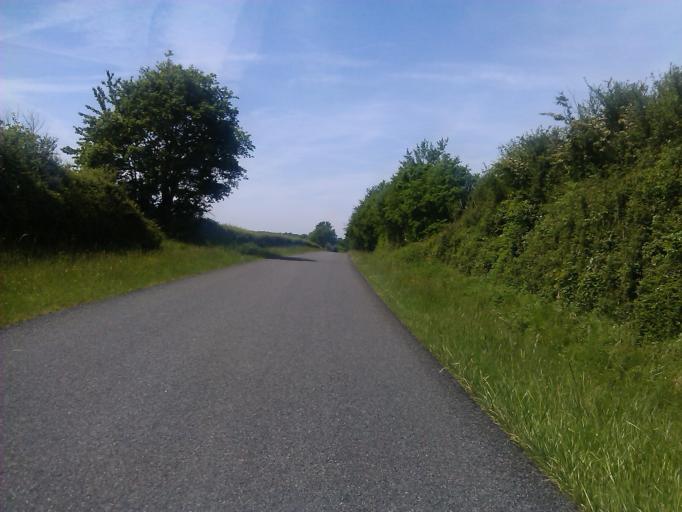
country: FR
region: Centre
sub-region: Departement du Cher
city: Le Chatelet
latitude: 46.5837
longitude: 2.4143
